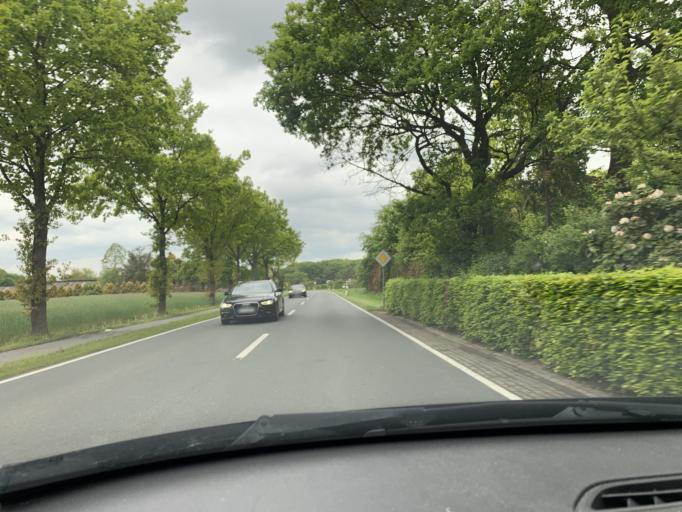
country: DE
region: Lower Saxony
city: Bad Zwischenahn
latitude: 53.1918
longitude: 8.0546
